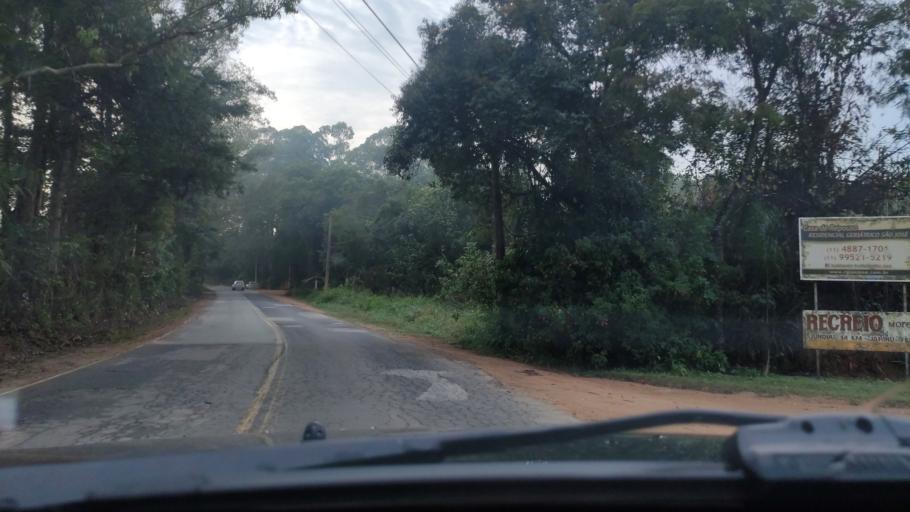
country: BR
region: Sao Paulo
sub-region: Campo Limpo Paulista
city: Campo Limpo Paulista
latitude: -23.1389
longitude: -46.7938
